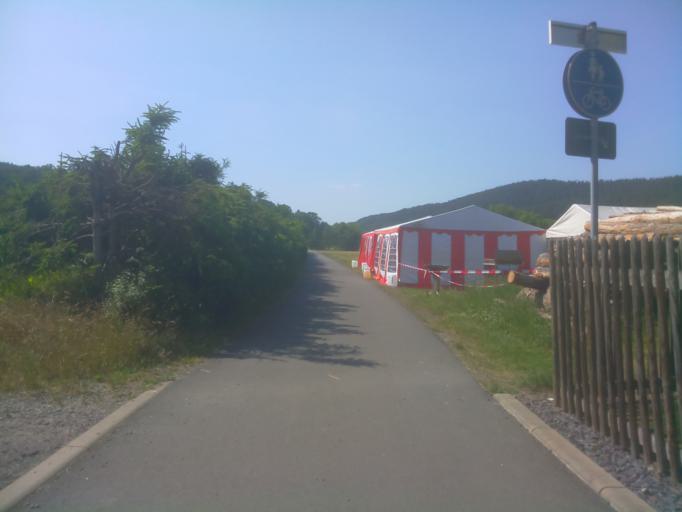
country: DE
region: Thuringia
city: Langenorla
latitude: 50.7329
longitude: 11.5949
